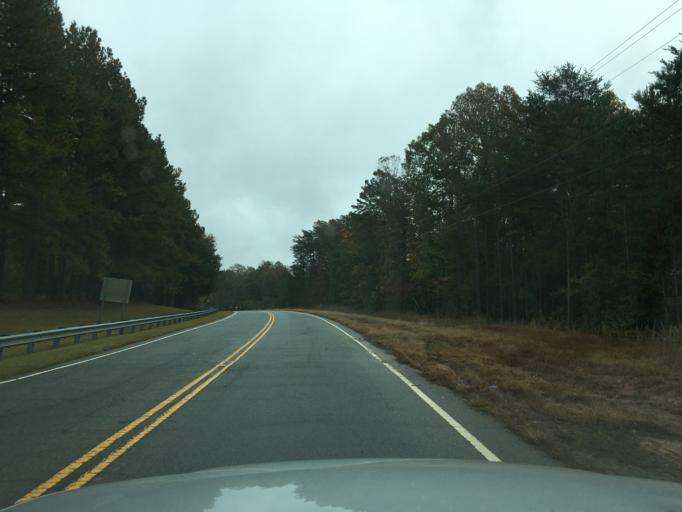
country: US
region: South Carolina
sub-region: Pickens County
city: Clemson
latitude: 34.7884
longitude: -82.8892
